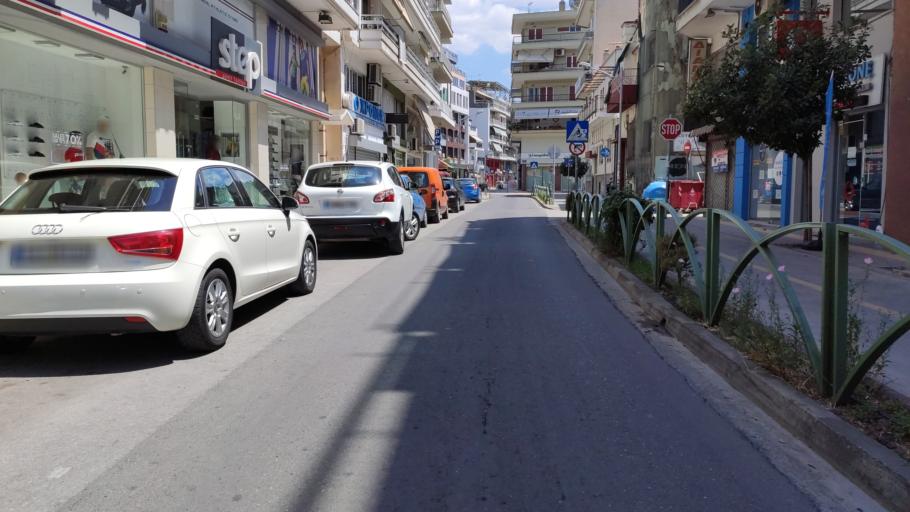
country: GR
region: East Macedonia and Thrace
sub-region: Nomos Rodopis
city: Komotini
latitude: 41.1160
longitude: 25.4040
